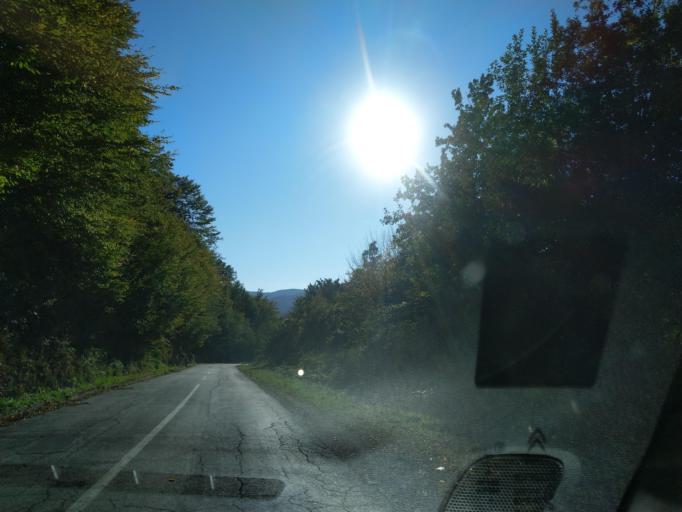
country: RS
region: Central Serbia
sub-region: Moravicki Okrug
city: Ivanjica
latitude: 43.4737
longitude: 20.2447
